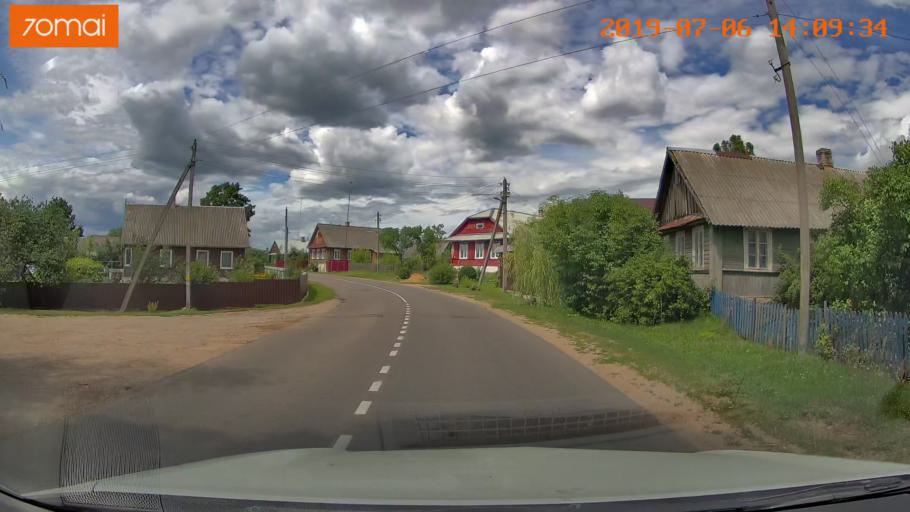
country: BY
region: Minsk
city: Ivyanyets
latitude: 53.8826
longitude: 26.7481
